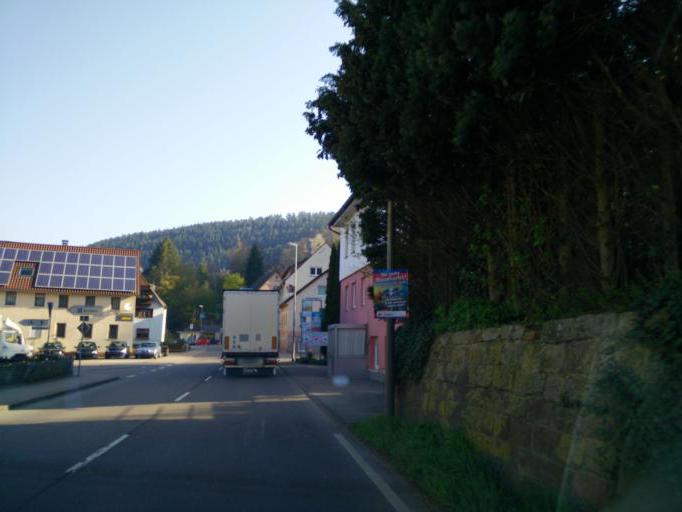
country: DE
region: Baden-Wuerttemberg
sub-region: Karlsruhe Region
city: Calw
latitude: 48.7334
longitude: 8.7360
